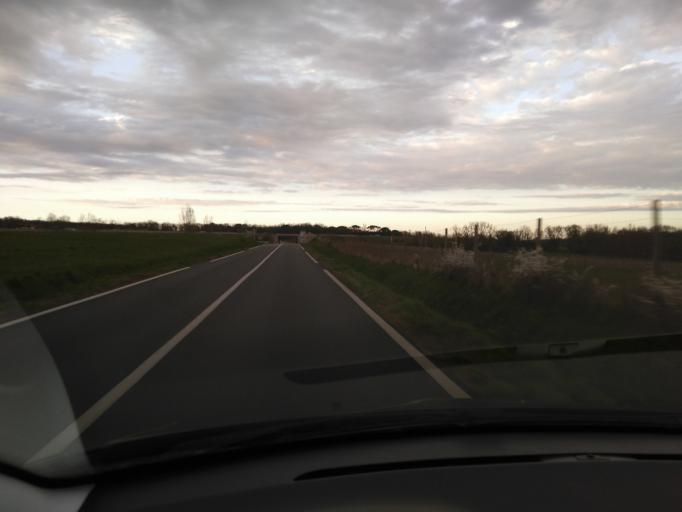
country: FR
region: Midi-Pyrenees
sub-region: Departement de la Haute-Garonne
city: La Salvetat-Saint-Gilles
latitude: 43.5841
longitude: 1.2681
